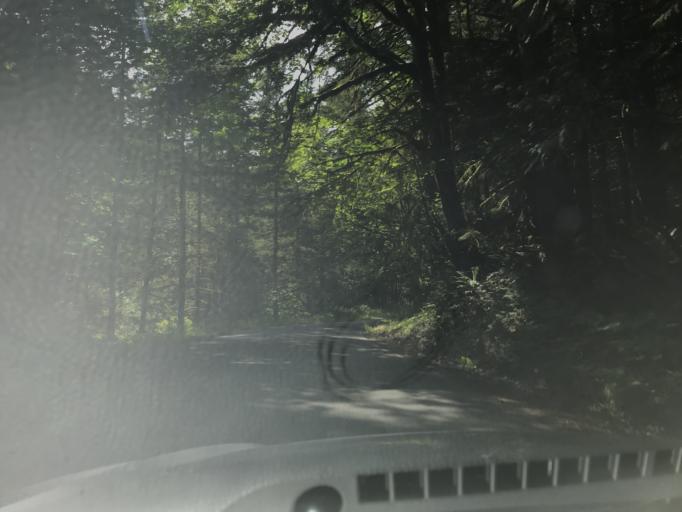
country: US
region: Washington
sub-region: King County
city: Hobart
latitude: 47.4154
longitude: -121.9296
